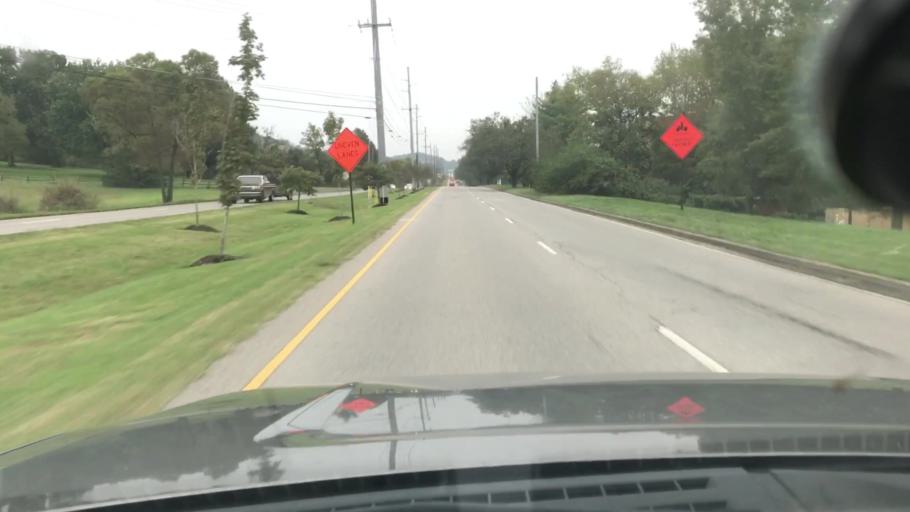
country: US
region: Tennessee
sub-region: Williamson County
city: Brentwood
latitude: 36.0388
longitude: -86.8092
